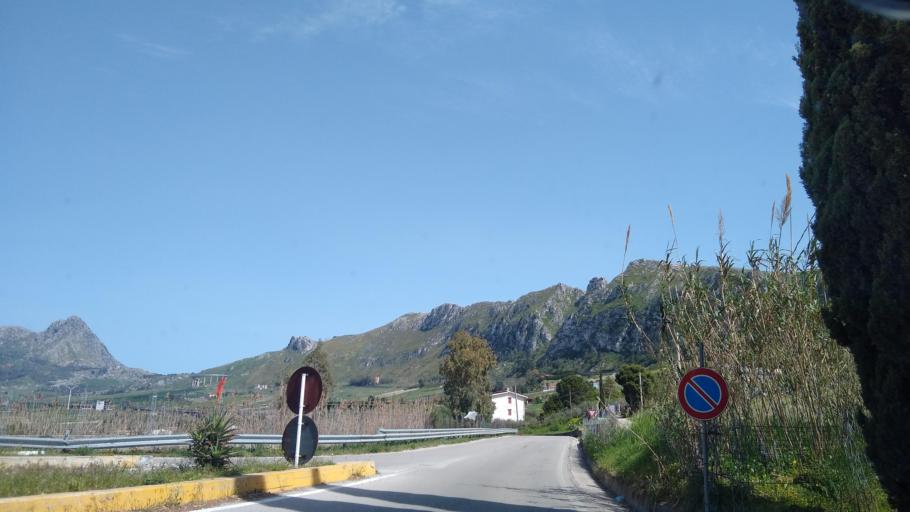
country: IT
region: Sicily
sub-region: Palermo
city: San Giuseppe Jato
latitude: 37.9757
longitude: 13.2011
